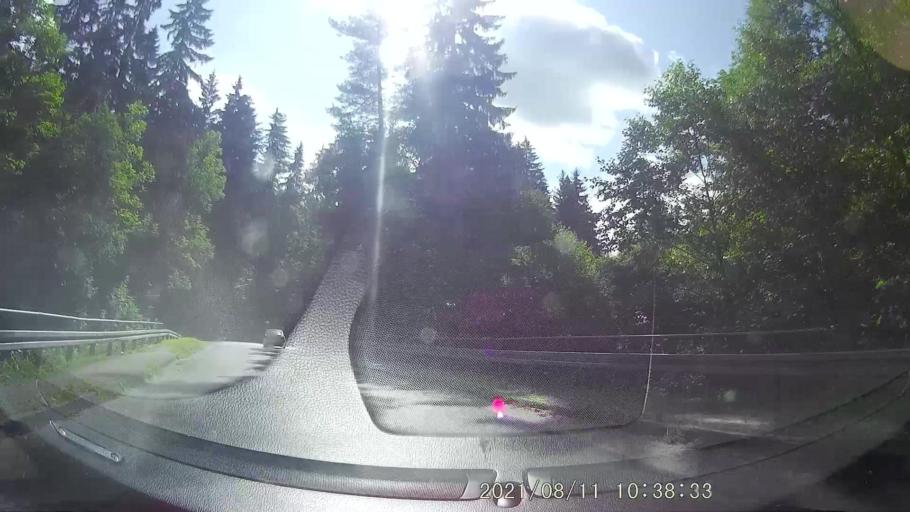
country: PL
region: Lower Silesian Voivodeship
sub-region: Powiat klodzki
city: Polanica-Zdroj
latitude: 50.4007
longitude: 16.4853
